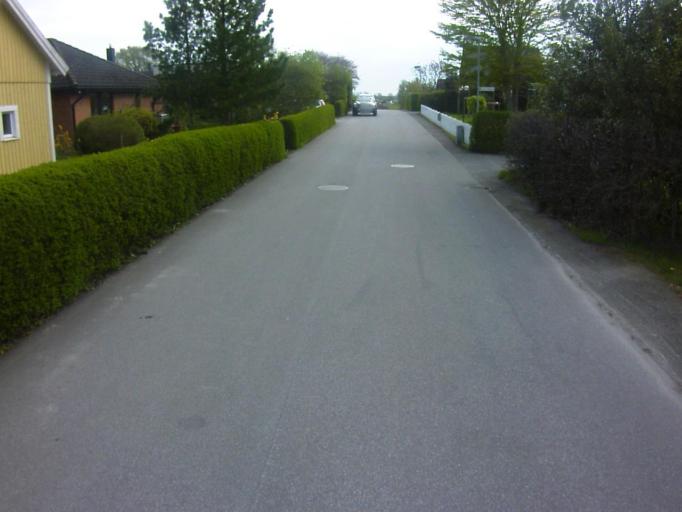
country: SE
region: Skane
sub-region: Kavlinge Kommun
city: Loddekopinge
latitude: 55.7587
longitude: 13.0191
